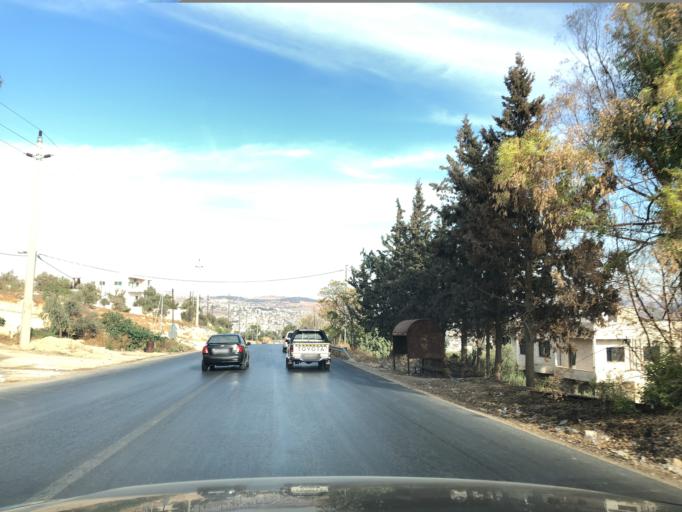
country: JO
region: Irbid
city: Al Kittah
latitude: 32.2807
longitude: 35.8618
